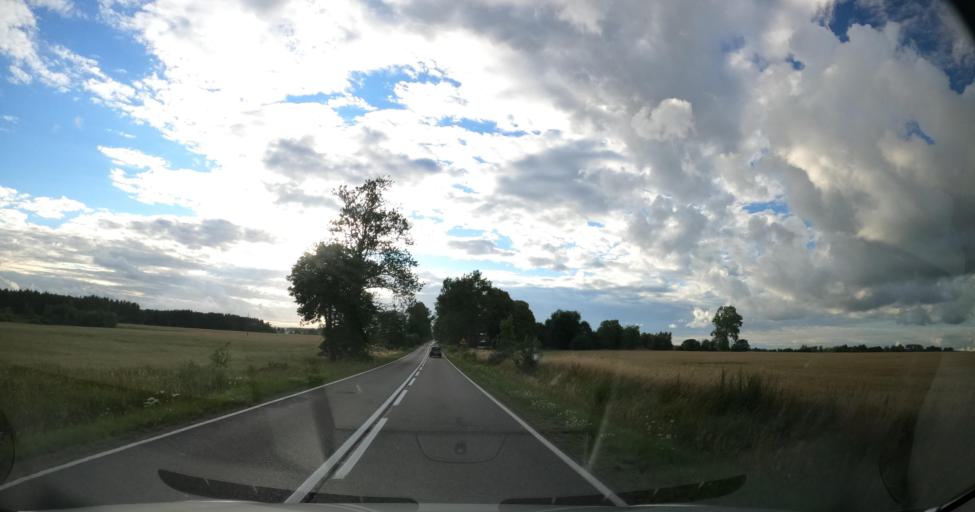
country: PL
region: Pomeranian Voivodeship
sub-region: Powiat slupski
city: Damnica
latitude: 54.4320
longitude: 17.3602
